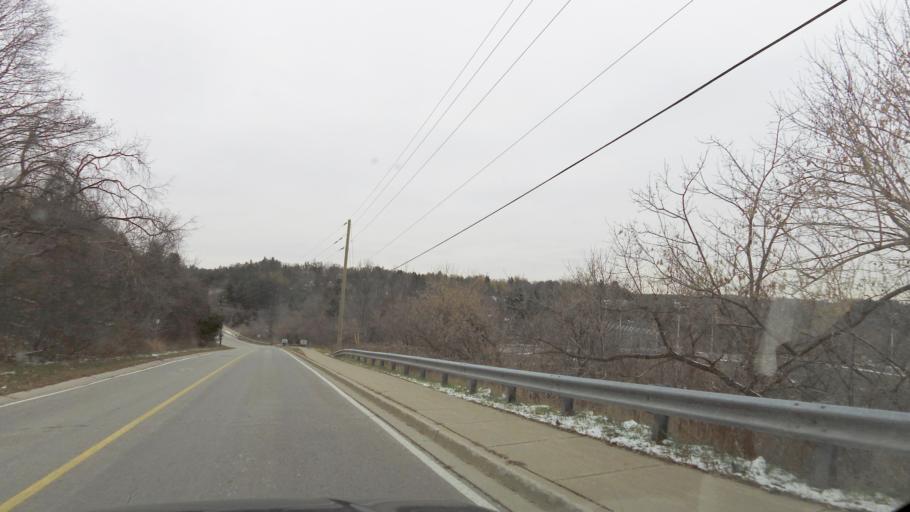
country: CA
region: Ontario
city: Vaughan
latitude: 43.8440
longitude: -79.6252
